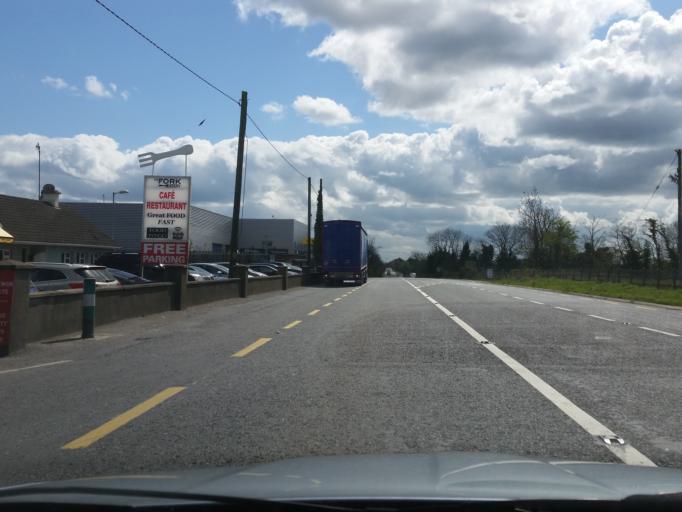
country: IE
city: Kentstown
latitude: 53.6661
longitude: -6.5299
